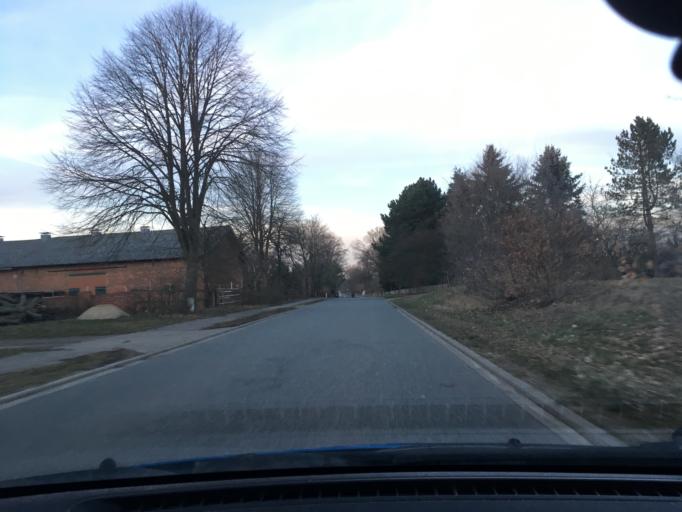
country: DE
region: Schleswig-Holstein
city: Langenlehsten
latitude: 53.5020
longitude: 10.7413
